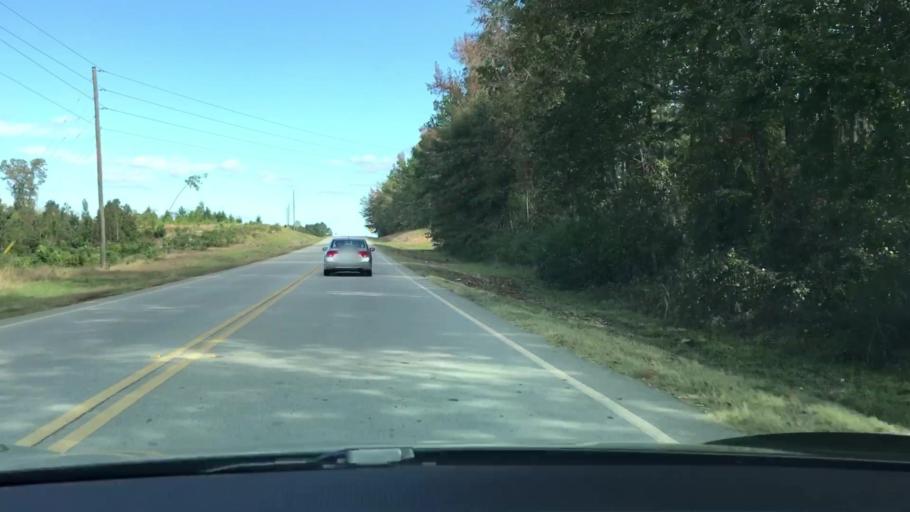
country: US
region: Georgia
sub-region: Jefferson County
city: Wrens
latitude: 33.2251
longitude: -82.4618
